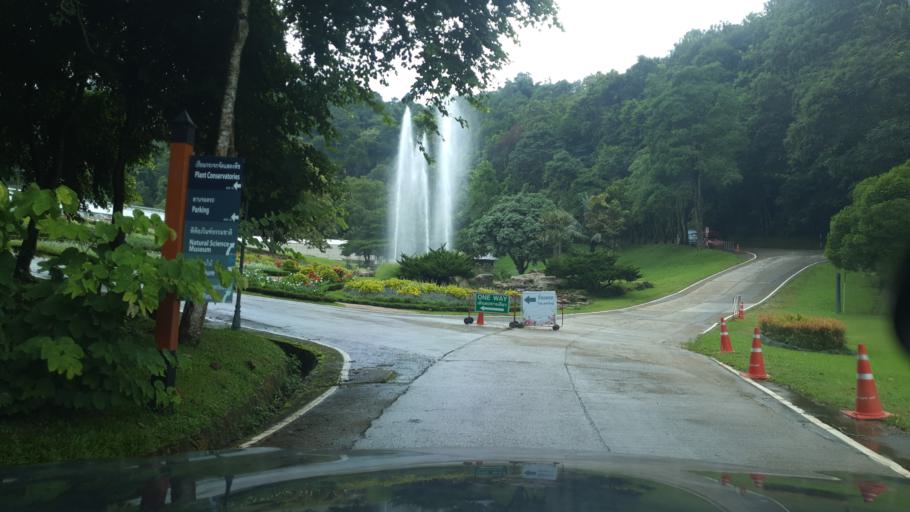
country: TH
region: Chiang Mai
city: Samoeng
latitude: 18.8890
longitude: 98.8614
